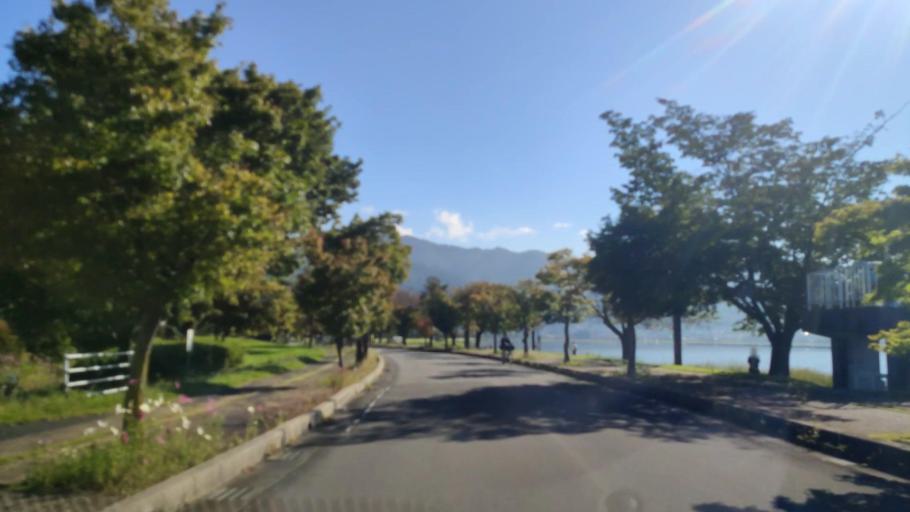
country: JP
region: Nagano
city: Suwa
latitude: 36.0637
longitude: 138.0853
